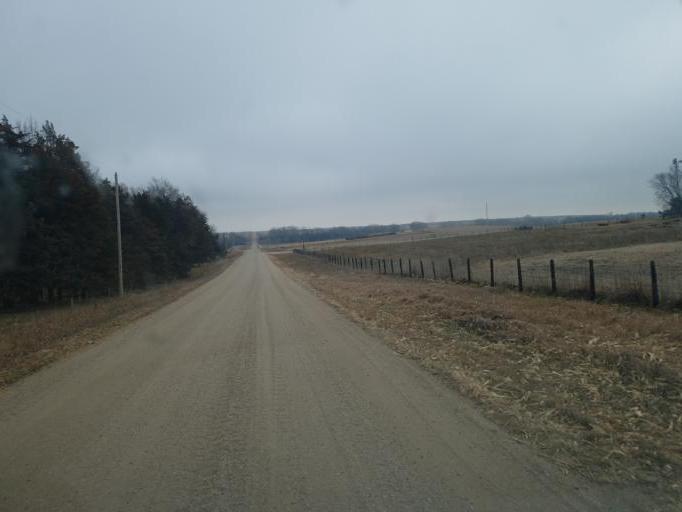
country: US
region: Nebraska
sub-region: Knox County
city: Center
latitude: 42.5392
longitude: -97.8010
